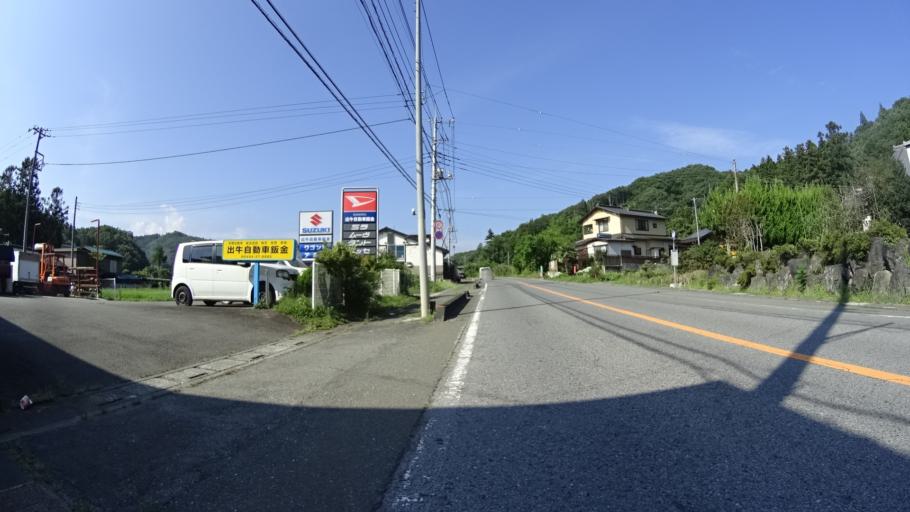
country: JP
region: Saitama
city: Chichibu
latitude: 36.0243
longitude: 139.0689
